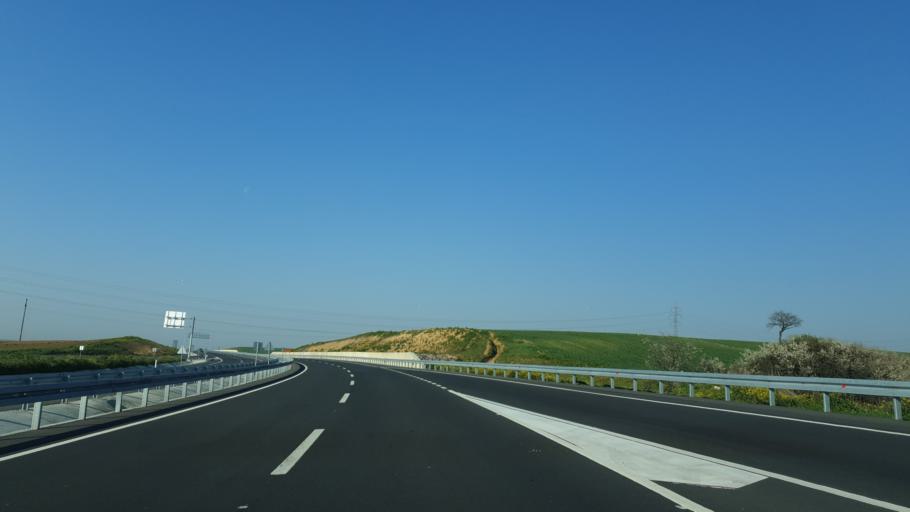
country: TR
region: Tekirdag
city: Marmaracik
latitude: 41.1990
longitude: 27.7561
